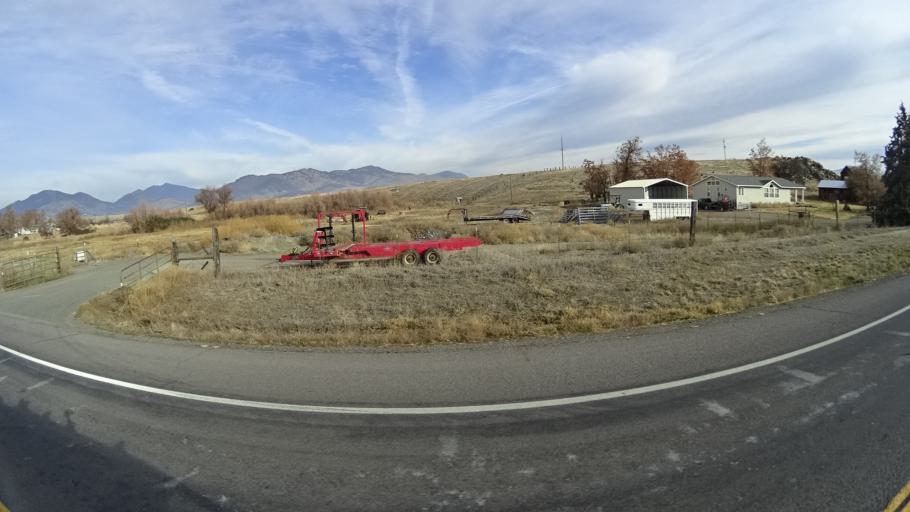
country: US
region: California
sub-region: Siskiyou County
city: Montague
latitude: 41.7259
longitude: -122.5573
